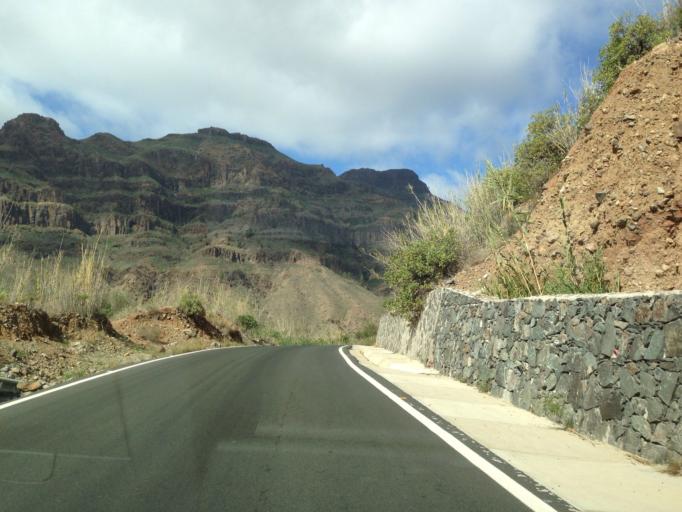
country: ES
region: Canary Islands
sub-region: Provincia de Las Palmas
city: Santa Lucia
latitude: 27.8736
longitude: -15.5651
